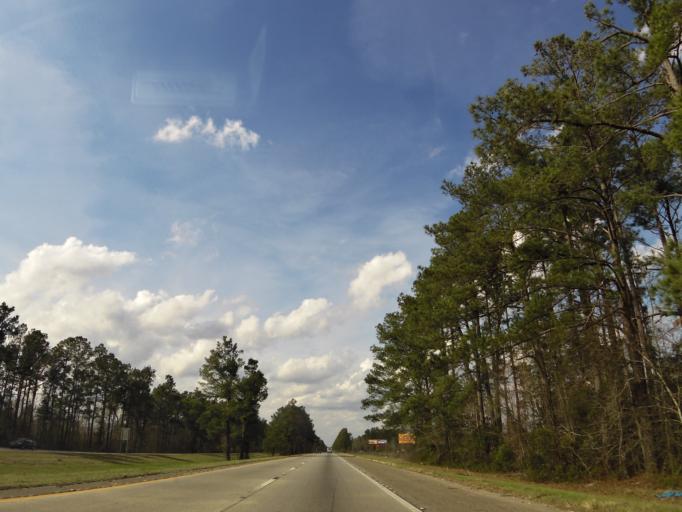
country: US
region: South Carolina
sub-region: Dorchester County
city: Ridgeville
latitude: 33.1887
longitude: -80.3872
